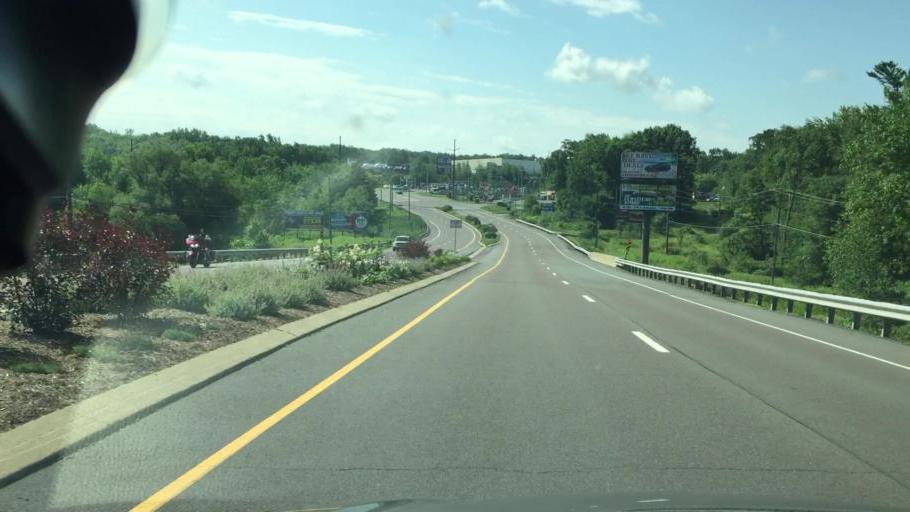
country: US
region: Pennsylvania
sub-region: Luzerne County
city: West Hazleton
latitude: 40.9743
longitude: -76.0109
